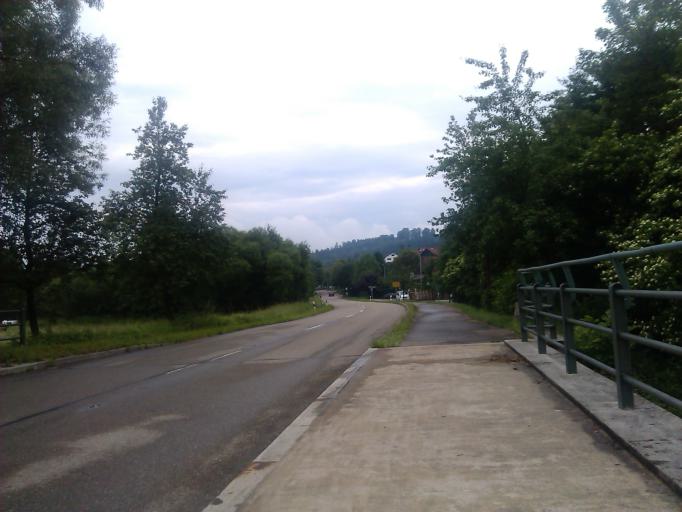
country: DE
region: Baden-Wuerttemberg
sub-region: Regierungsbezirk Stuttgart
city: Oberrot
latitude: 49.0194
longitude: 9.6606
